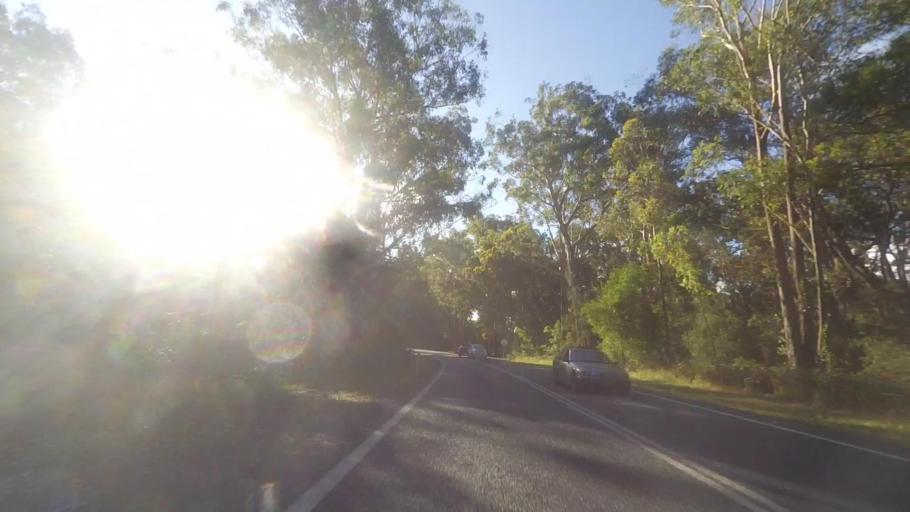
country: AU
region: New South Wales
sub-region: Great Lakes
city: Nabiac
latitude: -32.0895
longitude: 152.4656
